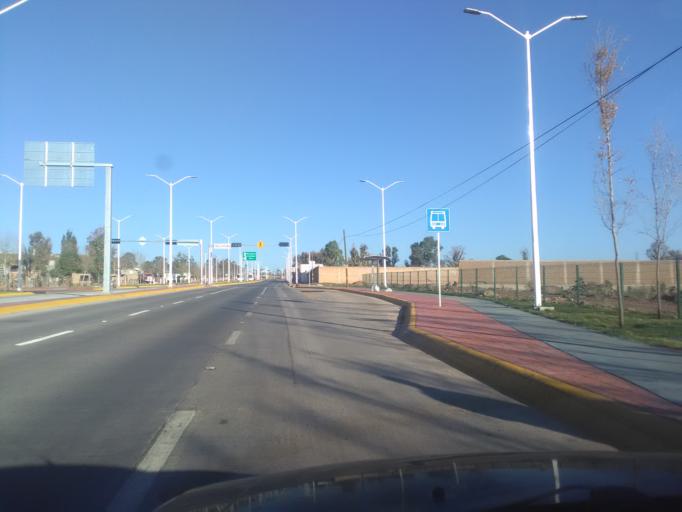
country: MX
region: Durango
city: Victoria de Durango
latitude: 23.9933
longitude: -104.7138
